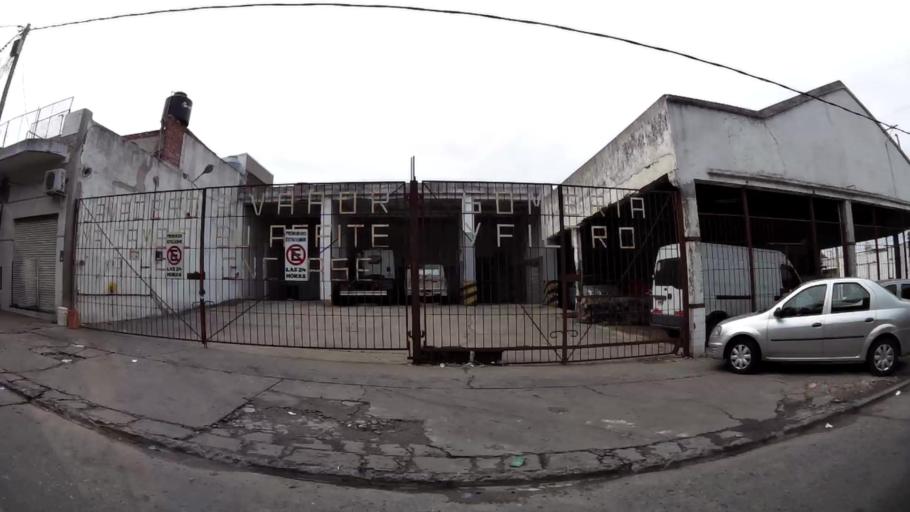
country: AR
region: Buenos Aires F.D.
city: Villa Lugano
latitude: -34.6995
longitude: -58.5073
